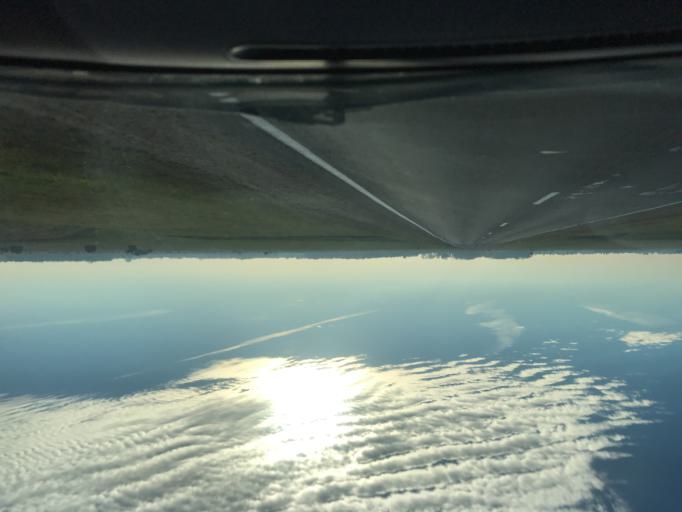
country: BY
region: Brest
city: Drahichyn
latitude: 52.2132
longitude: 25.1906
